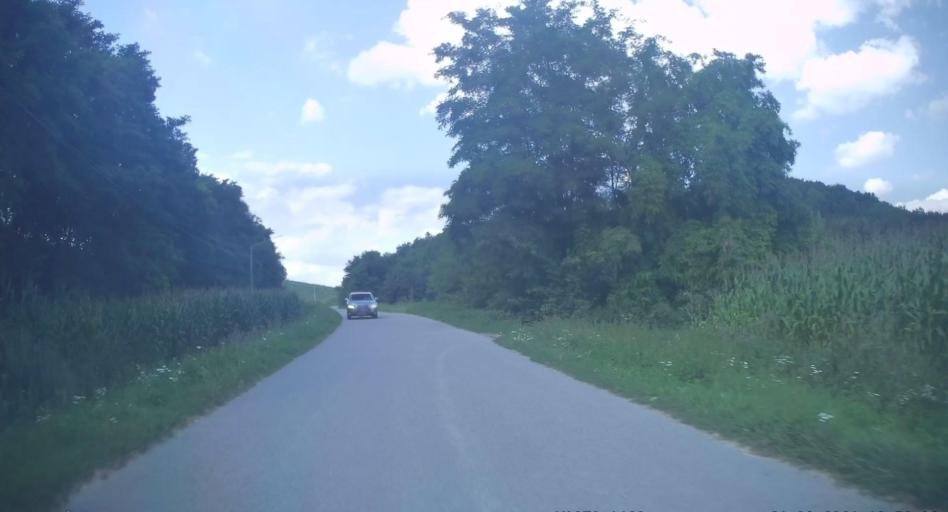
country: PL
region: Lesser Poland Voivodeship
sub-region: Powiat bochenski
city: Dziewin
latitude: 50.1496
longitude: 20.4644
